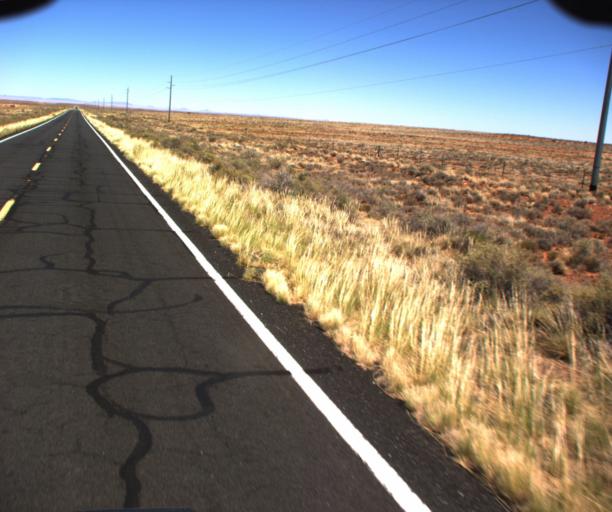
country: US
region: Arizona
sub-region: Coconino County
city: LeChee
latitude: 34.8888
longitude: -110.8718
